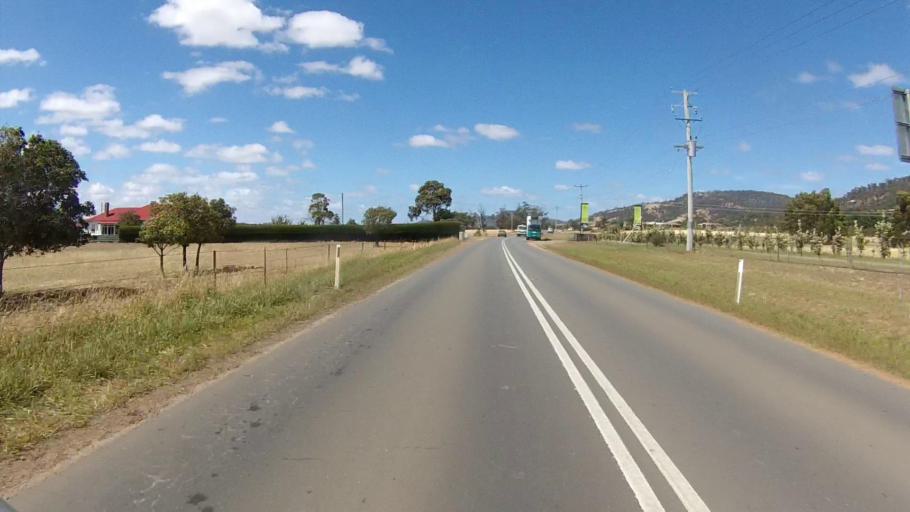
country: AU
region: Tasmania
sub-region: Clarence
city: Cambridge
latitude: -42.7753
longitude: 147.4163
